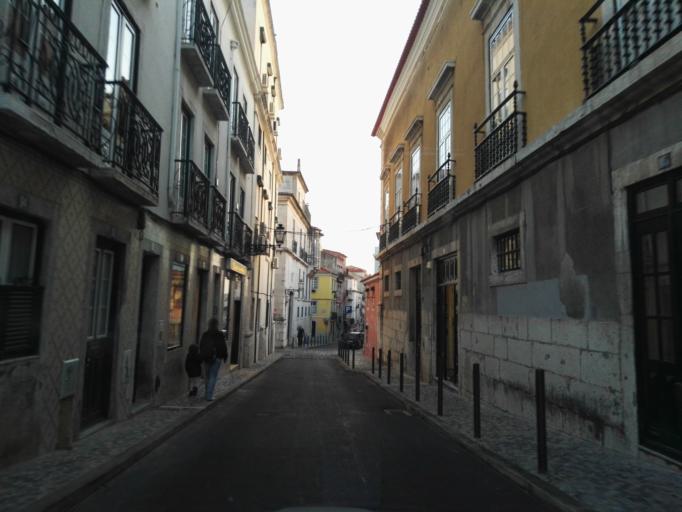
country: PT
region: Lisbon
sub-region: Lisbon
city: Lisbon
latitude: 38.7127
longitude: -9.1512
